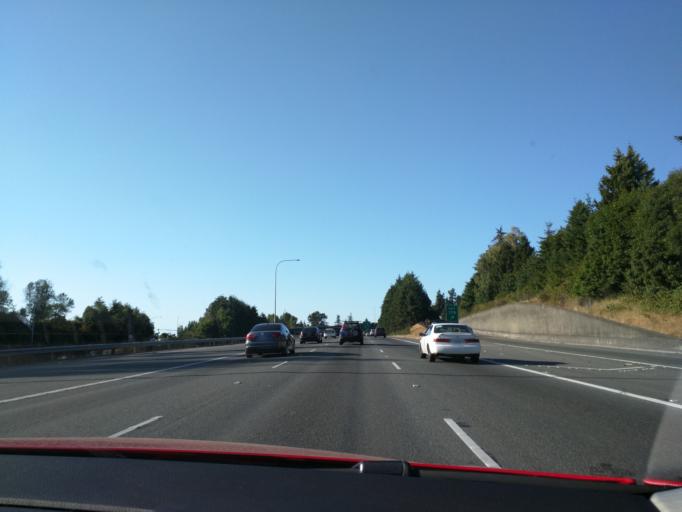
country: US
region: Washington
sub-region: Snohomish County
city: Mountlake Terrace
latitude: 47.7963
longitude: -122.3151
